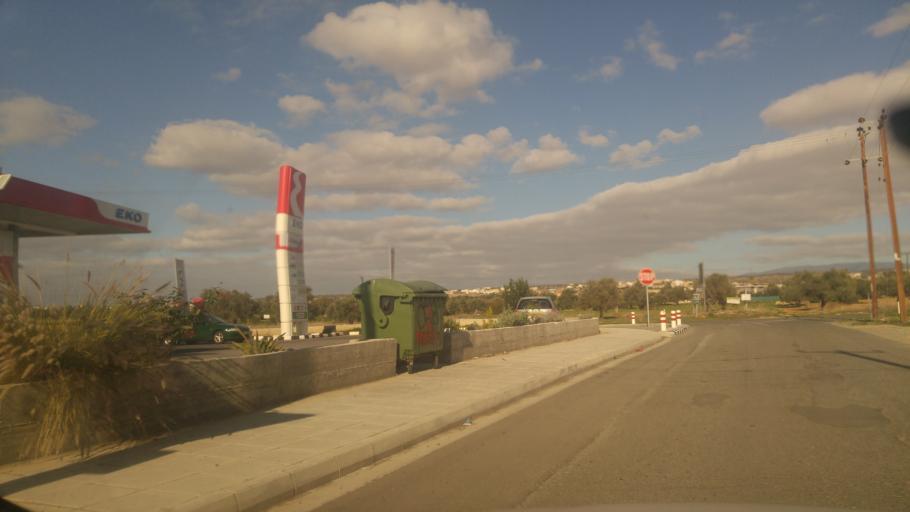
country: CY
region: Limassol
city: Ypsonas
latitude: 34.6824
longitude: 32.9527
